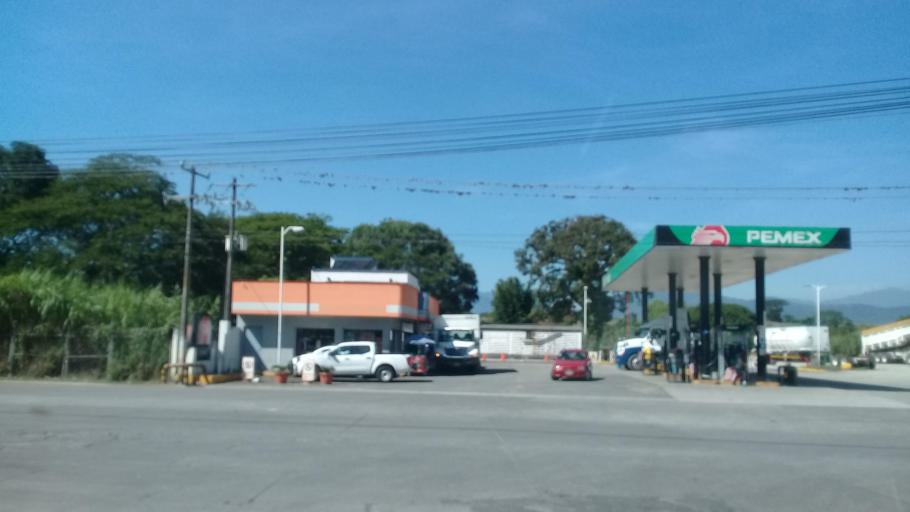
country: MX
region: Veracruz
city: Amatlan de los Reyes
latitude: 18.8569
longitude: -96.9125
